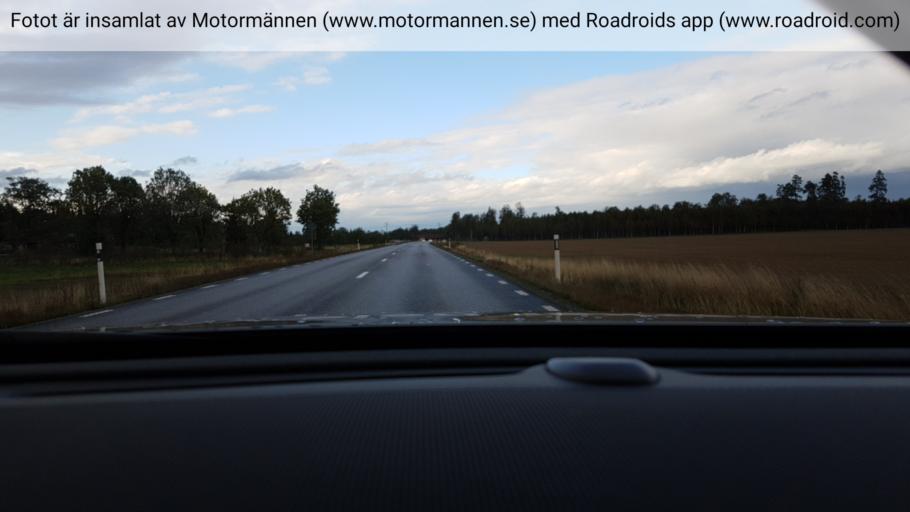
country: SE
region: Vaestra Goetaland
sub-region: Melleruds Kommun
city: Mellerud
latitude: 58.6514
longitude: 12.4137
